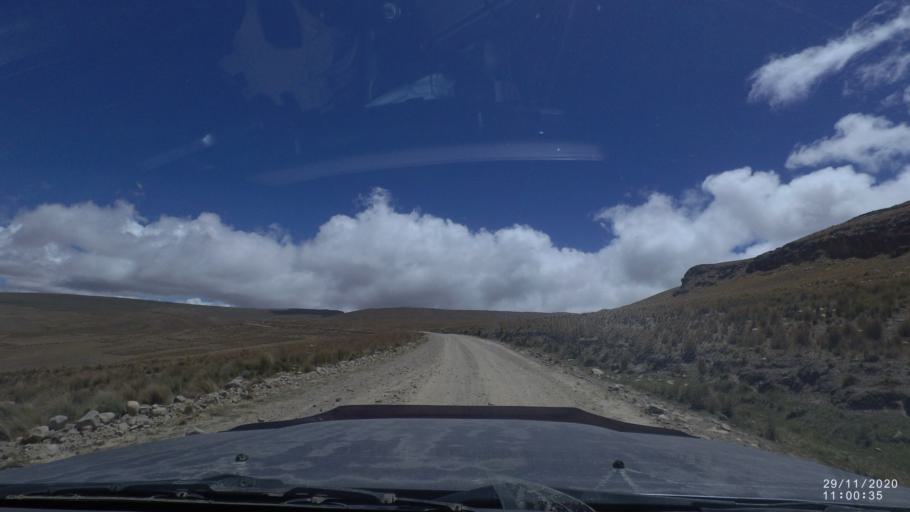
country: BO
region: Cochabamba
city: Cochabamba
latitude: -17.2035
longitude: -66.2254
